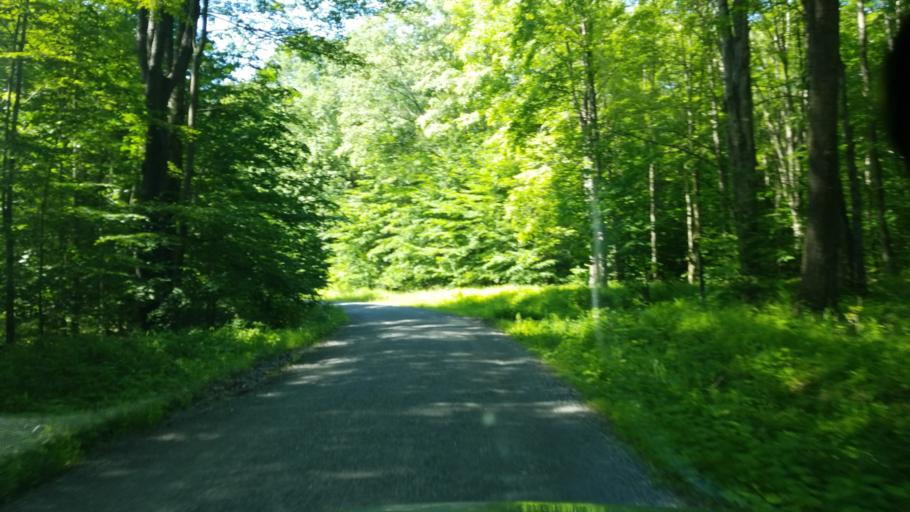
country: US
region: Pennsylvania
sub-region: Clearfield County
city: Clearfield
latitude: 41.2022
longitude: -78.4837
